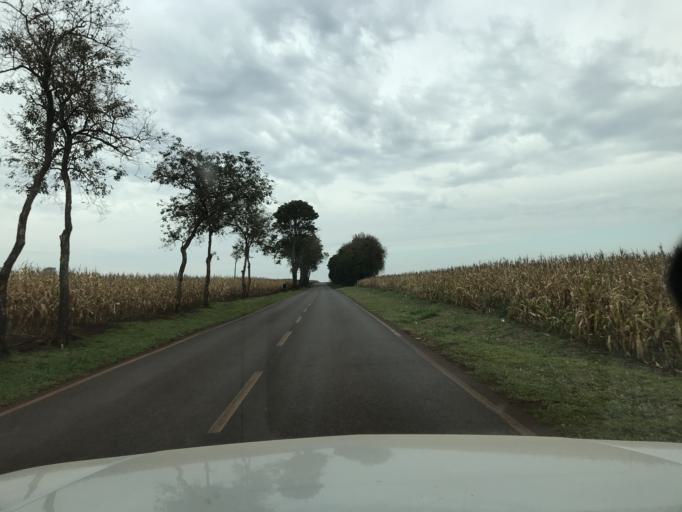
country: BR
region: Parana
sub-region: Palotina
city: Palotina
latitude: -24.4359
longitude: -53.9133
